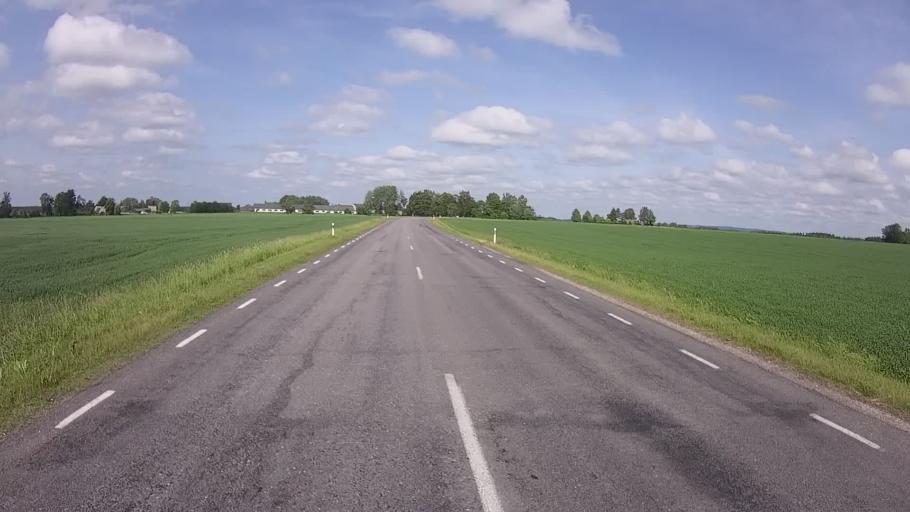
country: EE
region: Vorumaa
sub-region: Antsla vald
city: Vana-Antsla
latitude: 57.8952
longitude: 26.4919
